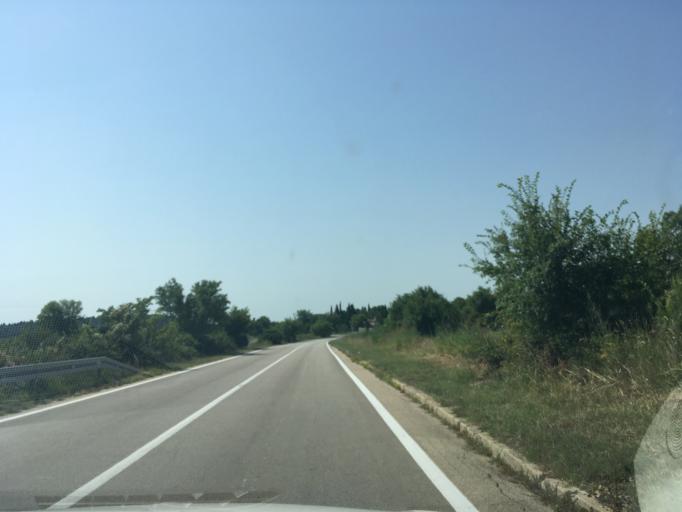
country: HR
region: Zadarska
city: Benkovac
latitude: 44.0236
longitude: 15.6194
